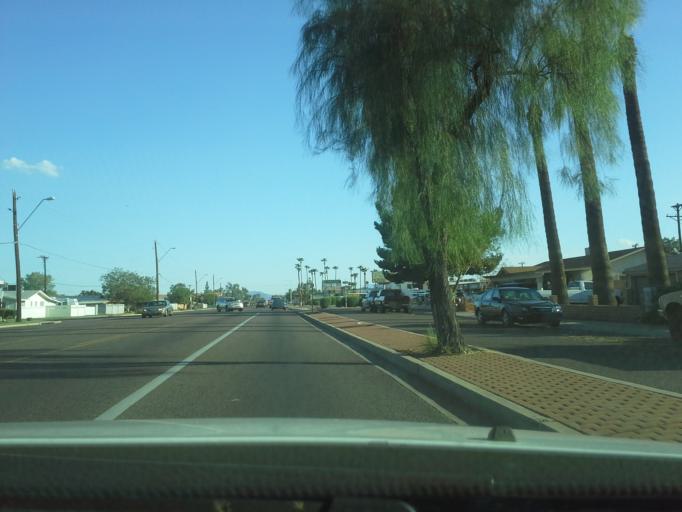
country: US
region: Arizona
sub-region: Maricopa County
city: Glendale
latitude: 33.5429
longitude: -112.1344
